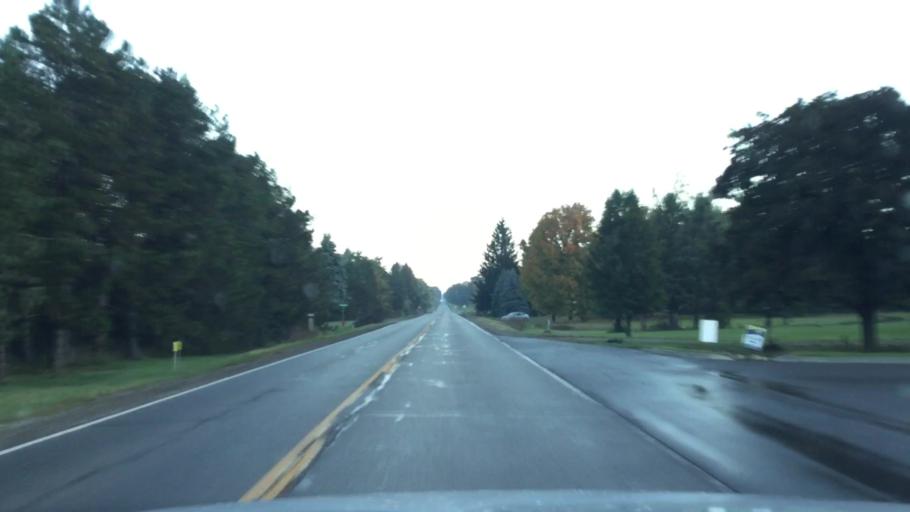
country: US
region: Michigan
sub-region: Livingston County
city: Howell
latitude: 42.6455
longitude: -83.9351
